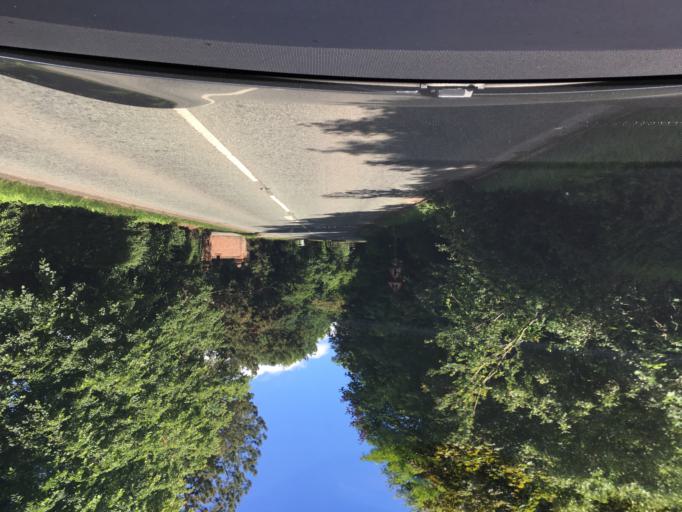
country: GB
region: England
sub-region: Cheshire East
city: Knutsford
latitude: 53.2888
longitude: -2.3428
